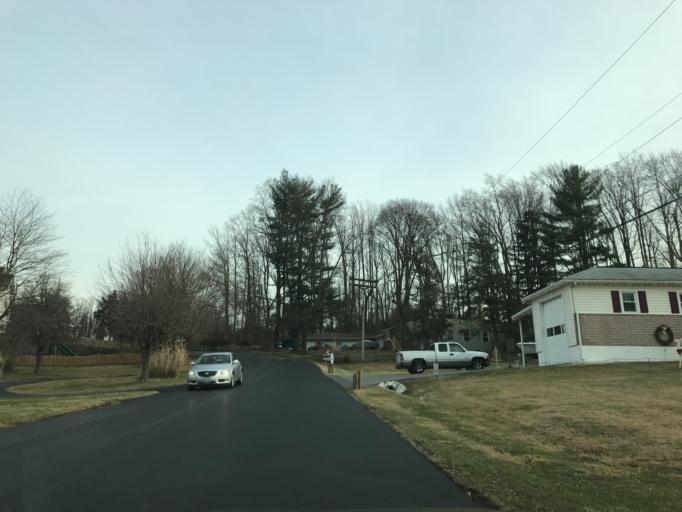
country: US
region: Maryland
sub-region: Baltimore County
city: White Marsh
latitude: 39.4109
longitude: -76.4094
